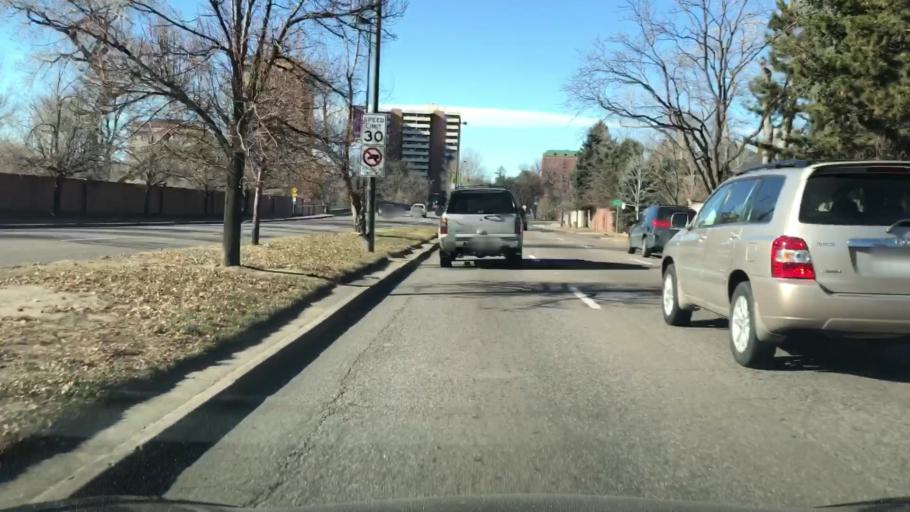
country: US
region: Colorado
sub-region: Denver County
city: Denver
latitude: 39.7183
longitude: -104.9698
